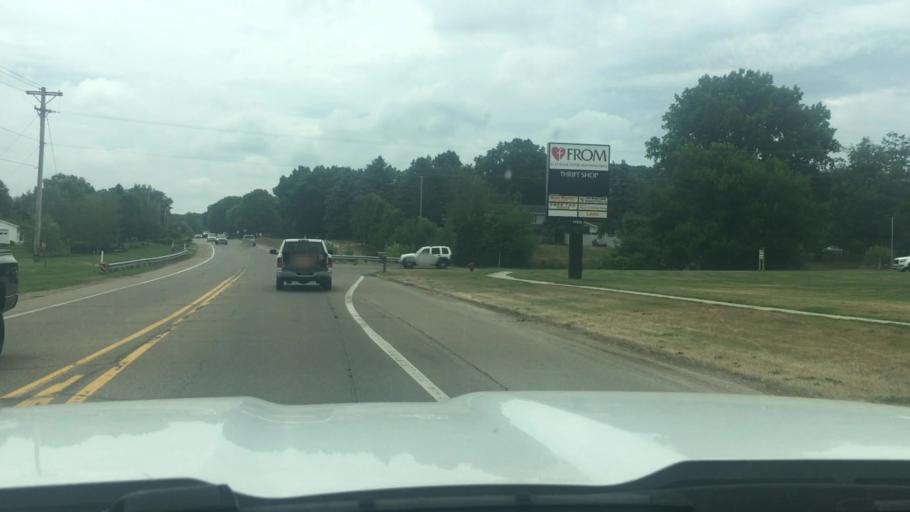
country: US
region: Michigan
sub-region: Kent County
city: Lowell
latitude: 42.9302
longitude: -85.3832
